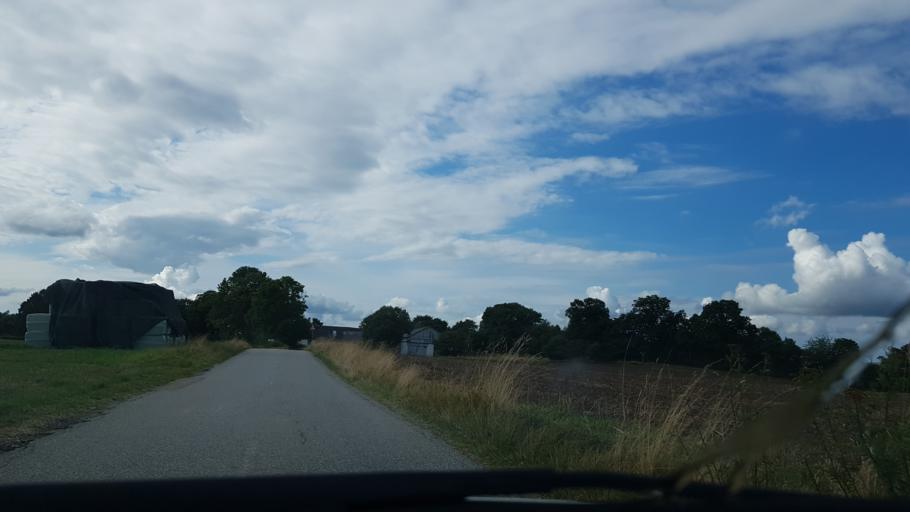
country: DK
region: Capital Region
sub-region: Fredensborg Kommune
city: Humlebaek
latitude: 55.9777
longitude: 12.4969
